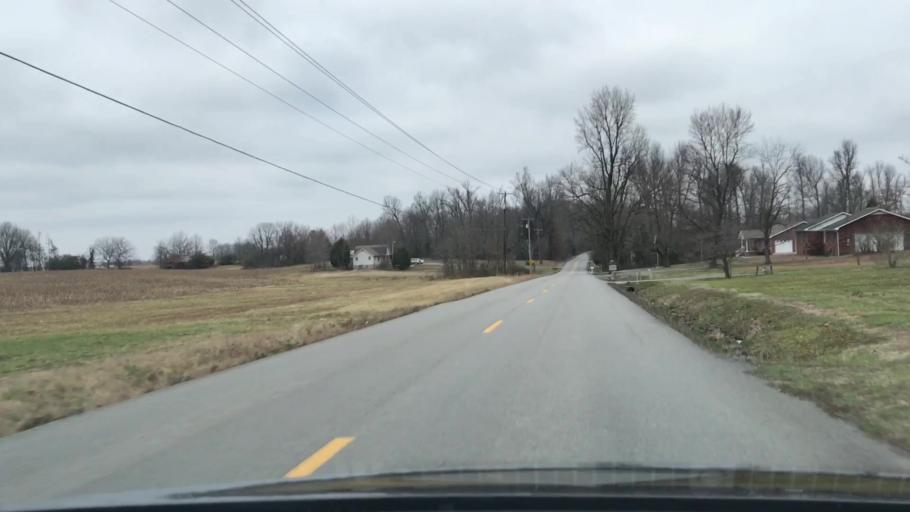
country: US
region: Kentucky
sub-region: Muhlenberg County
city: Morehead
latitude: 37.3607
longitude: -87.2328
